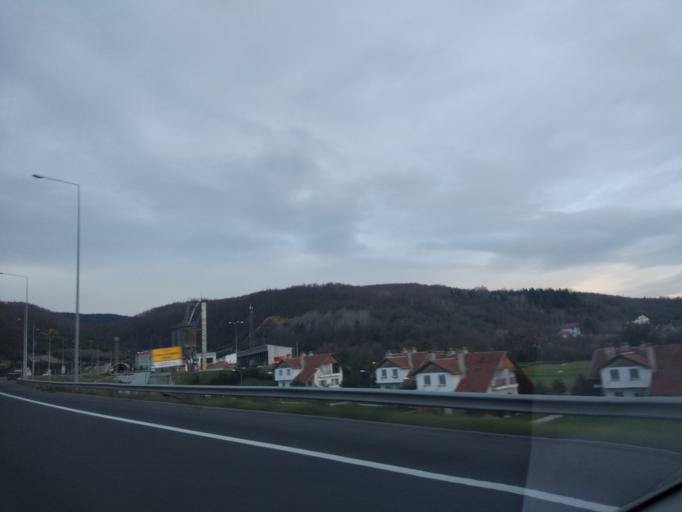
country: TR
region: Duzce
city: Kaynasli
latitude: 40.7328
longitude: 31.4451
